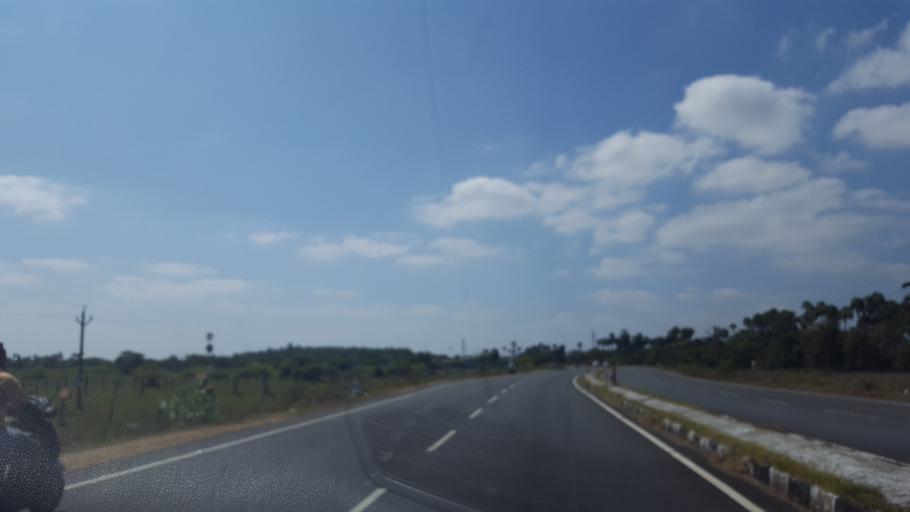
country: IN
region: Tamil Nadu
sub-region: Kancheepuram
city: Mamallapuram
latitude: 12.6229
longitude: 80.1704
